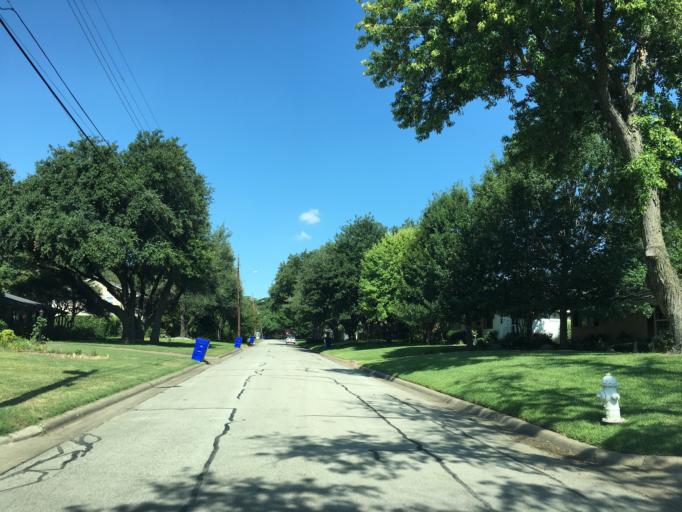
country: US
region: Texas
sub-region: Dallas County
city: Farmers Branch
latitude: 32.9190
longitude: -96.8740
